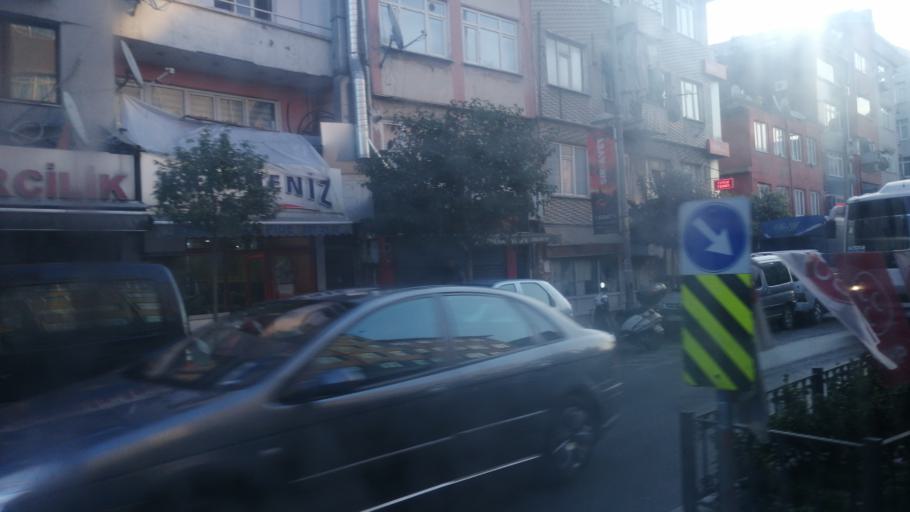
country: TR
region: Istanbul
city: Sisli
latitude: 41.0817
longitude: 28.9919
